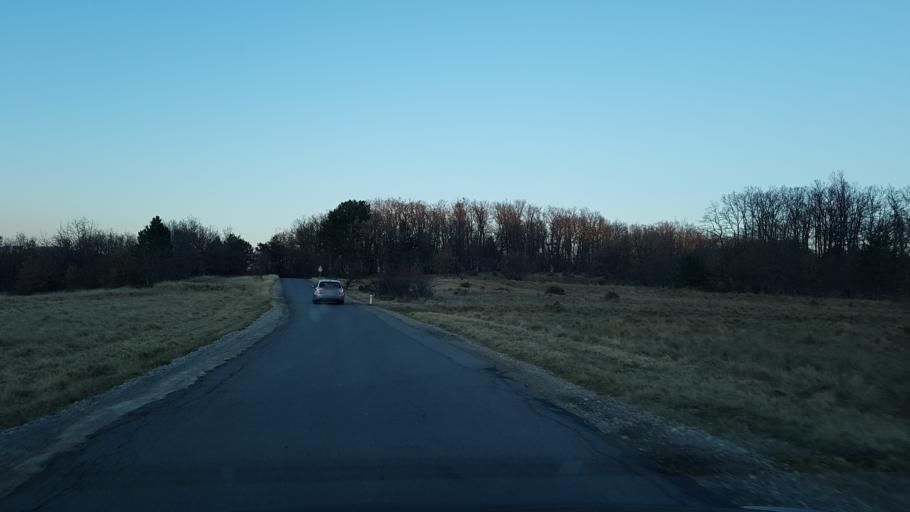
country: SI
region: Koper-Capodistria
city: Sv. Anton
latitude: 45.5082
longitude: 13.8628
